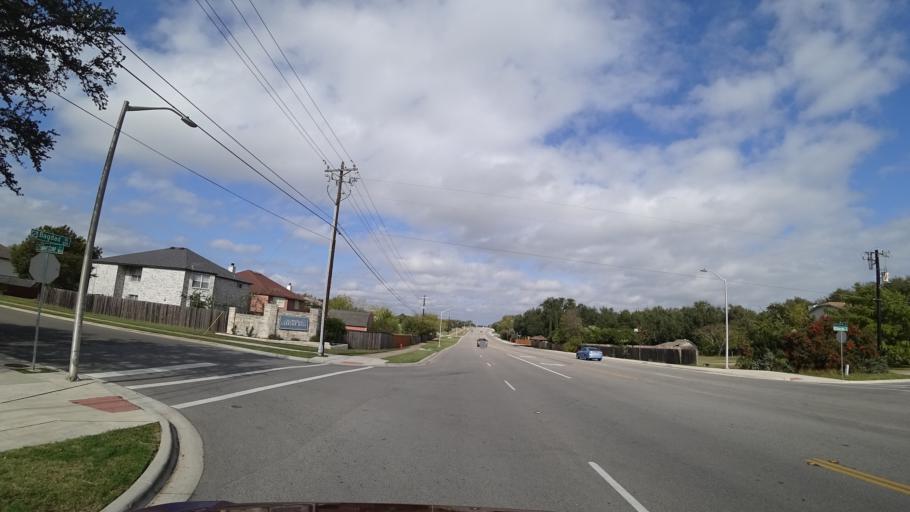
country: US
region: Texas
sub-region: Williamson County
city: Cedar Park
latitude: 30.5201
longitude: -97.8412
